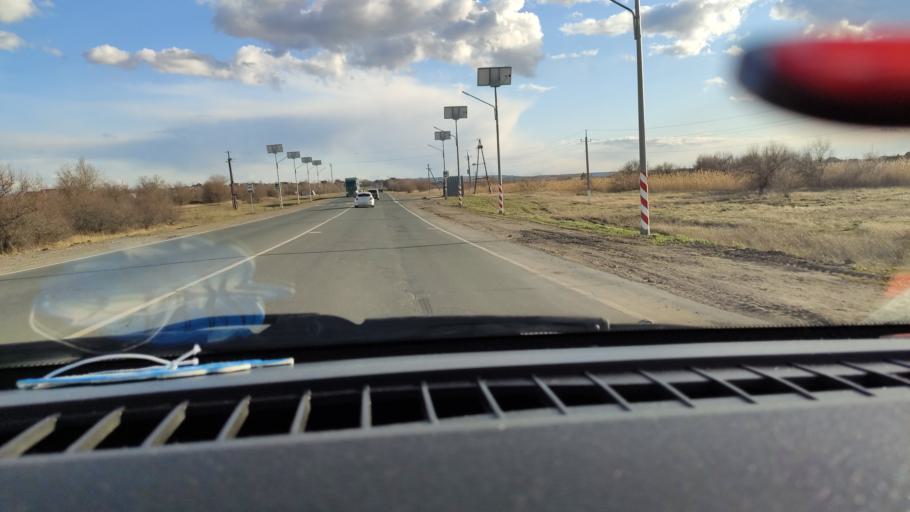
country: RU
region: Saratov
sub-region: Saratovskiy Rayon
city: Saratov
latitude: 51.6890
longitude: 46.0049
